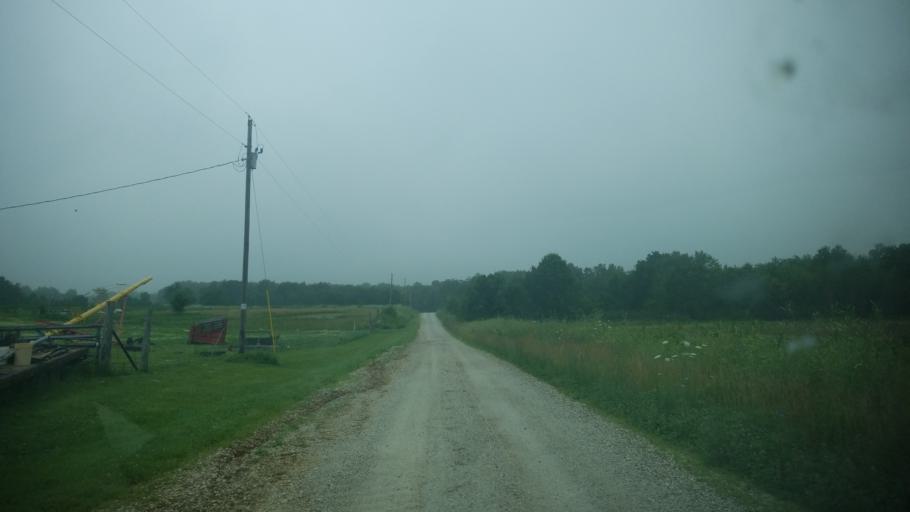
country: US
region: Missouri
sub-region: Audrain County
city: Vandalia
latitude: 39.2726
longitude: -91.3403
